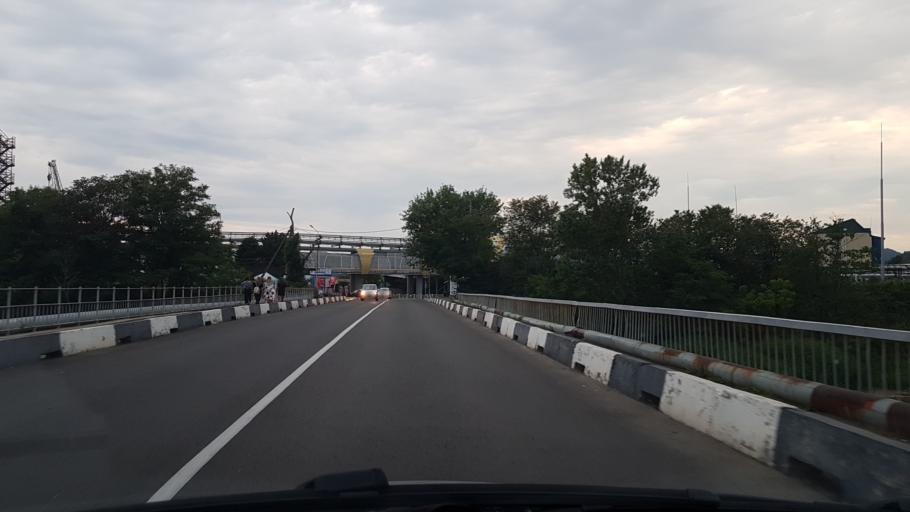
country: RU
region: Krasnodarskiy
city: Tuapse
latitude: 44.0901
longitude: 39.0826
